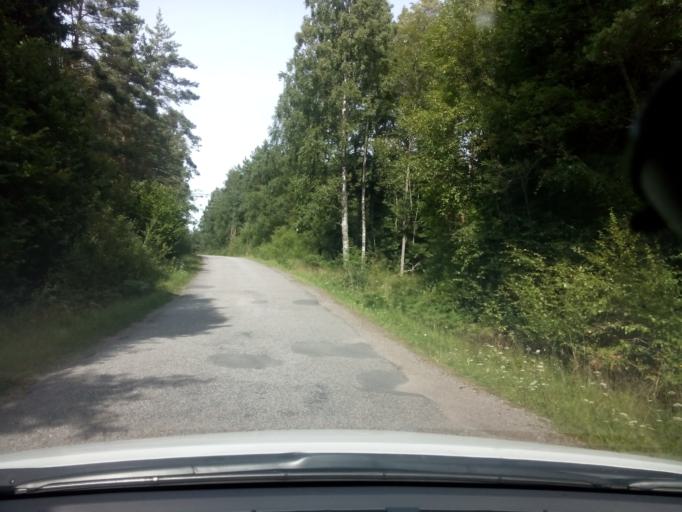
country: SE
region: Soedermanland
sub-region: Trosa Kommun
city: Trosa
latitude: 58.7601
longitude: 17.3700
